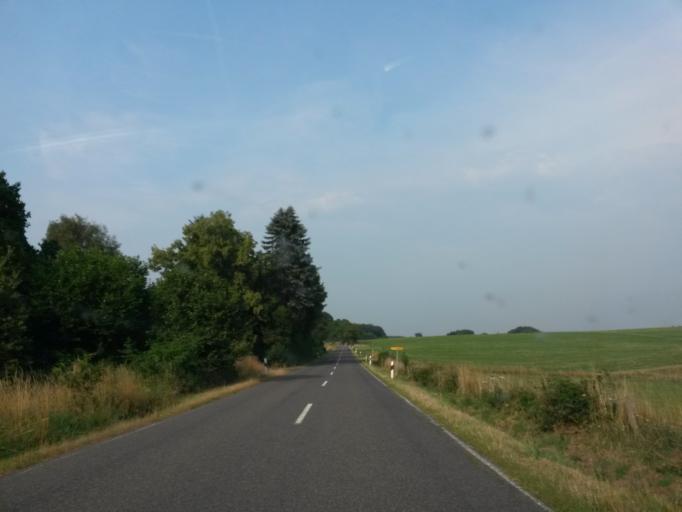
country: DE
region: North Rhine-Westphalia
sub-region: Regierungsbezirk Koln
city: Much
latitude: 50.8903
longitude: 7.4138
